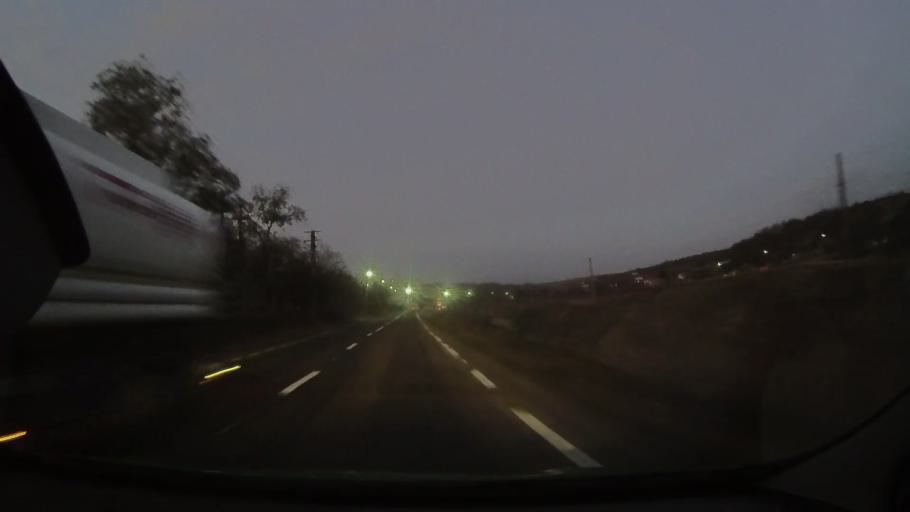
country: RO
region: Constanta
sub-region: Comuna Ion Corvin
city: Ion Corvin
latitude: 44.1080
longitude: 27.8019
